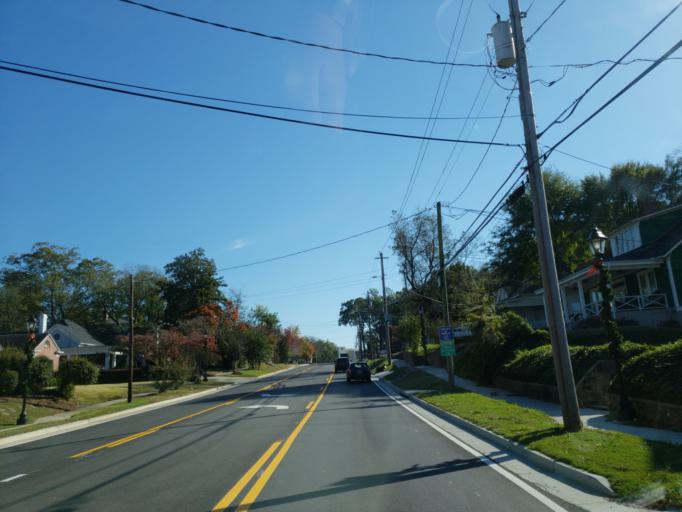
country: US
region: Georgia
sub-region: Gwinnett County
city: Lawrenceville
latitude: 33.9542
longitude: -83.9894
